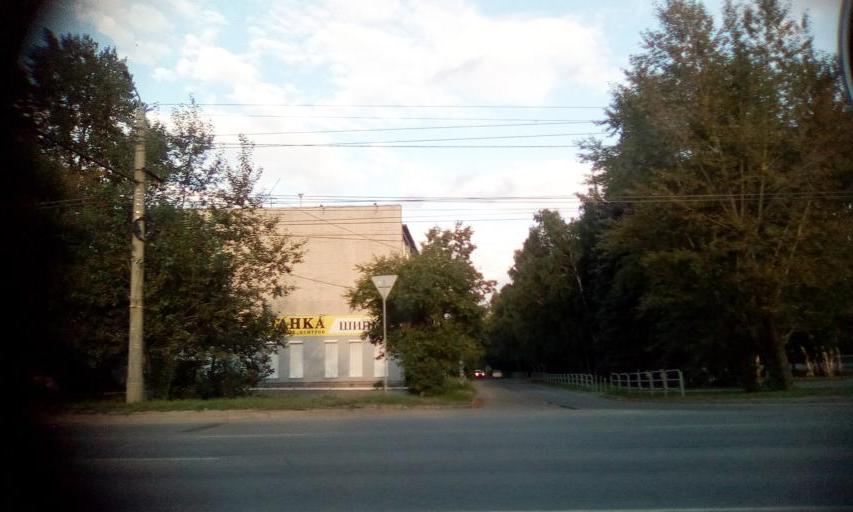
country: RU
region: Chelyabinsk
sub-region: Gorod Chelyabinsk
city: Chelyabinsk
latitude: 55.1194
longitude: 61.3624
